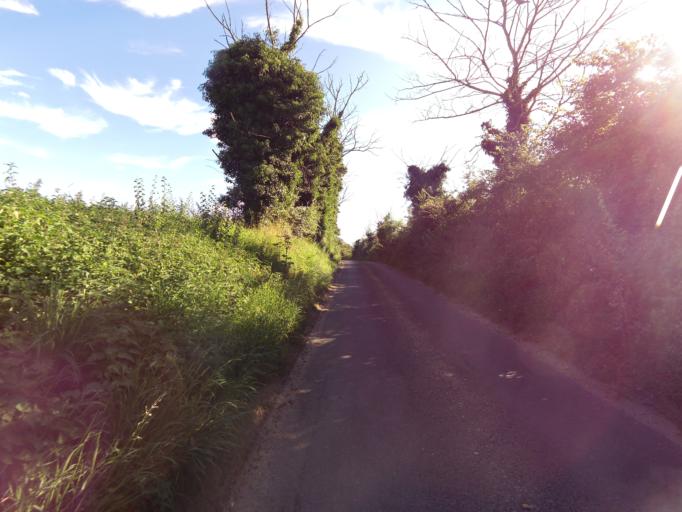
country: GB
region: England
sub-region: Suffolk
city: Kesgrave
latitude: 52.0367
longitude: 1.2542
